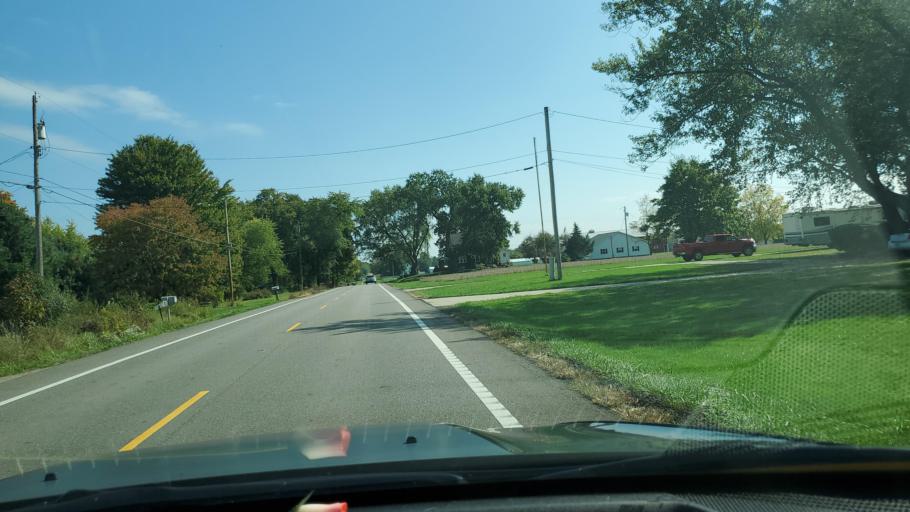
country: US
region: Ohio
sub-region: Trumbull County
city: Cortland
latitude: 41.3887
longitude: -80.6478
